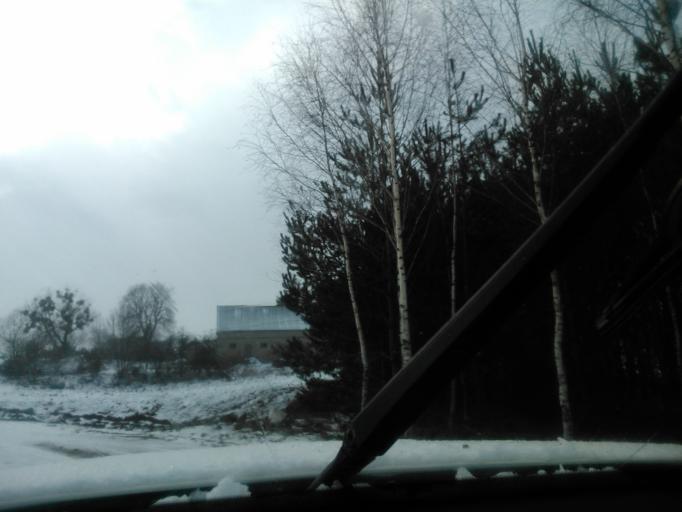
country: PL
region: Kujawsko-Pomorskie
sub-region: Powiat brodnicki
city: Bobrowo
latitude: 53.3117
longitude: 19.2497
